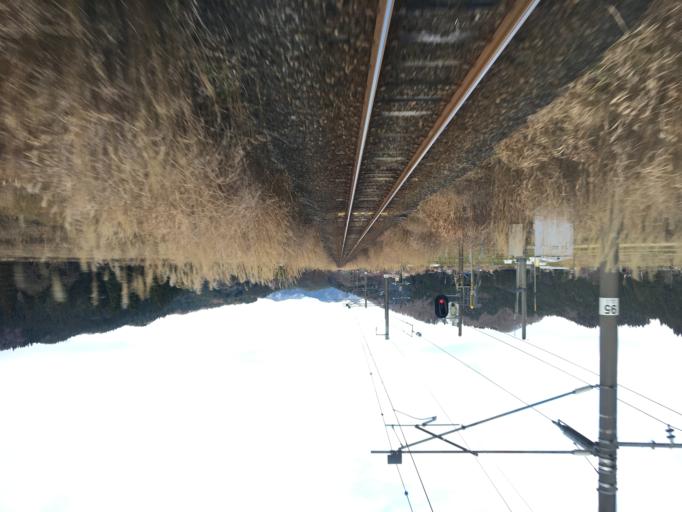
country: JP
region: Yamagata
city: Shinjo
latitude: 38.9657
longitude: 140.2999
